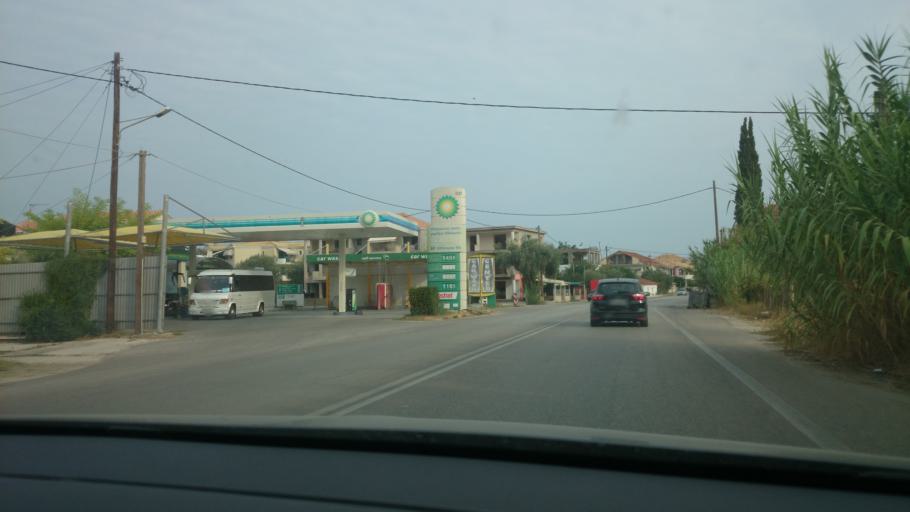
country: GR
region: Ionian Islands
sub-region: Lefkada
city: Lefkada
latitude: 38.8174
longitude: 20.7030
